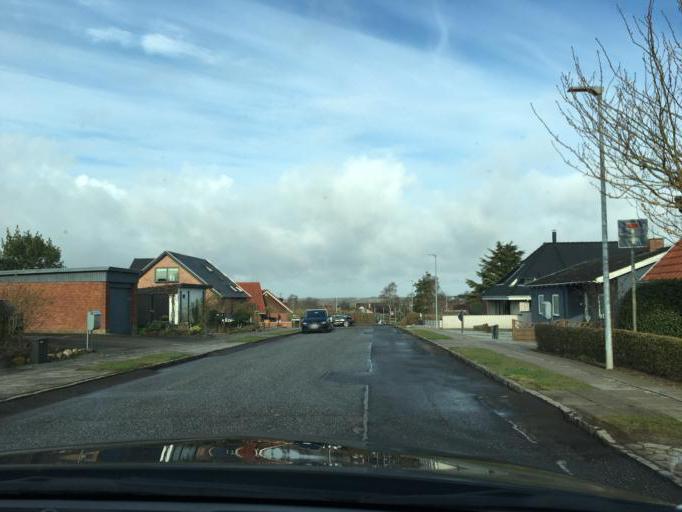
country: DK
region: South Denmark
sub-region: Kolding Kommune
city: Kolding
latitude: 55.4979
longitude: 9.4481
